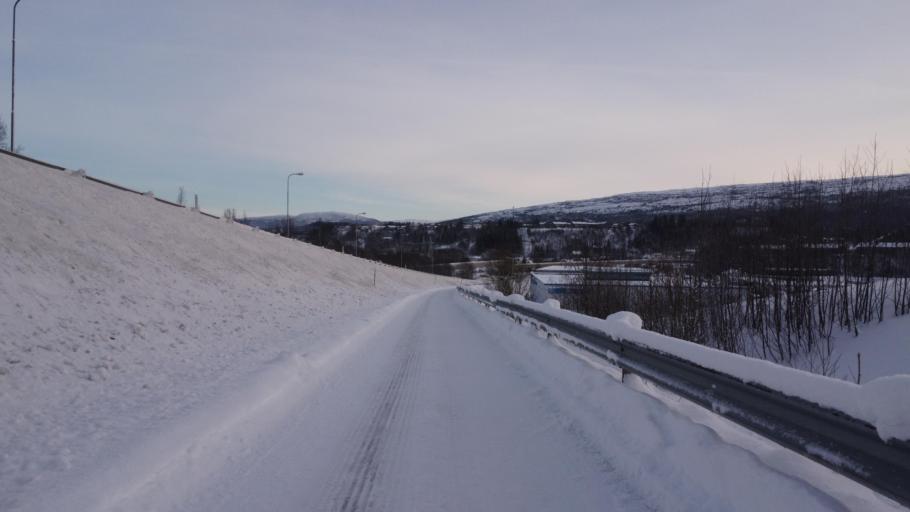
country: NO
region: Nordland
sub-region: Rana
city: Mo i Rana
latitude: 66.3239
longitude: 14.1615
